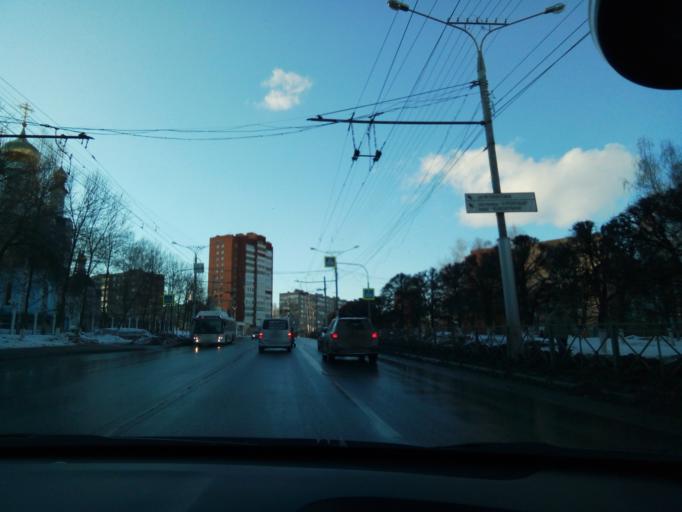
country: RU
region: Chuvashia
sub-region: Cheboksarskiy Rayon
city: Cheboksary
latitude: 56.1398
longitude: 47.1873
